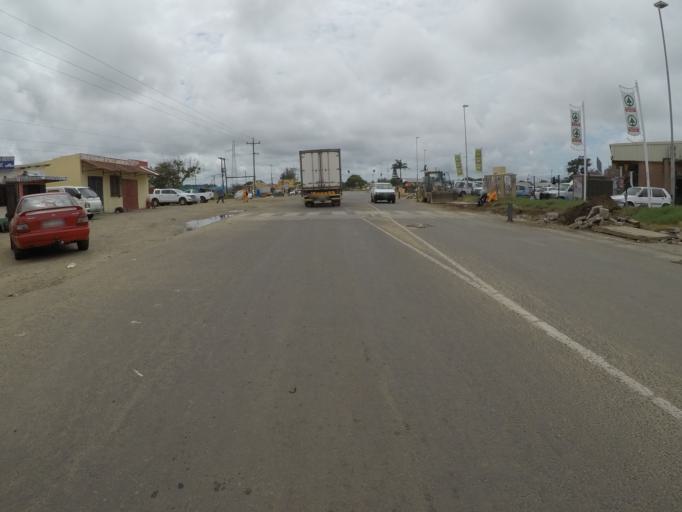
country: ZA
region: KwaZulu-Natal
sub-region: uThungulu District Municipality
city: eSikhawini
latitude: -28.8718
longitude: 31.8994
